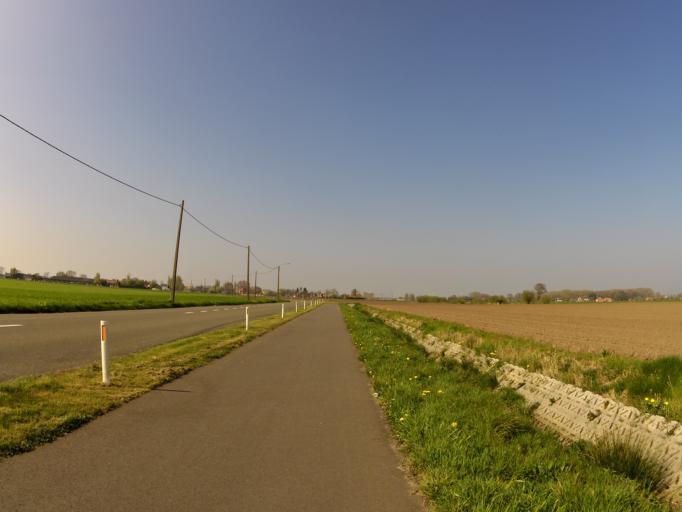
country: BE
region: Flanders
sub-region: Provincie West-Vlaanderen
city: Koekelare
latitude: 51.1137
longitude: 2.9662
